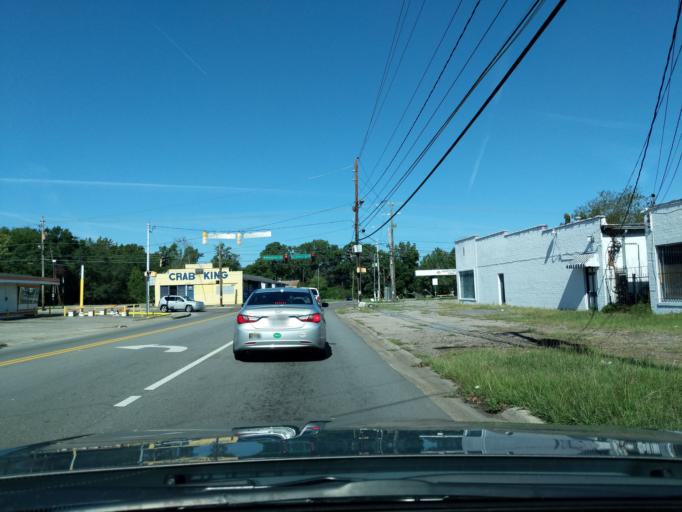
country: US
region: Georgia
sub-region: Richmond County
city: Augusta
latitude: 33.4474
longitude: -82.0065
